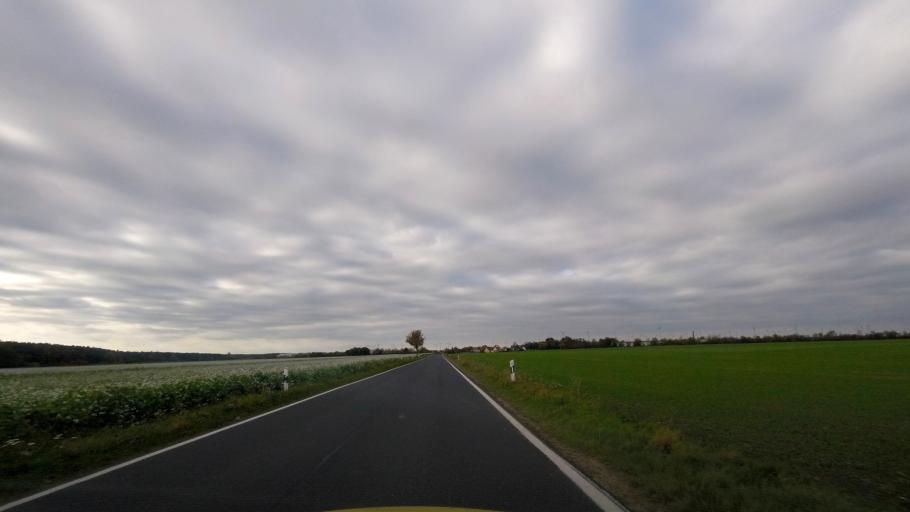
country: DE
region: Saxony-Anhalt
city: Seyda
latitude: 51.9637
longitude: 12.8711
